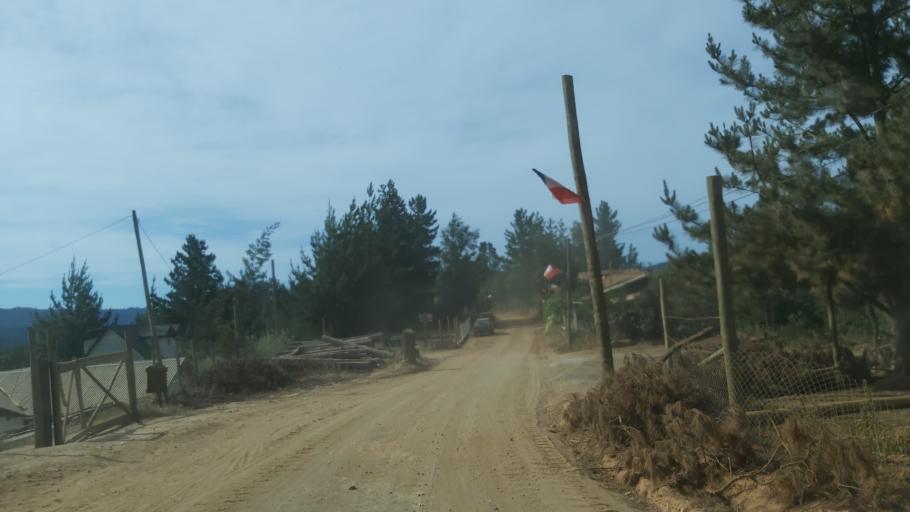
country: CL
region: Maule
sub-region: Provincia de Talca
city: Constitucion
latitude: -34.8455
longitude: -72.0380
